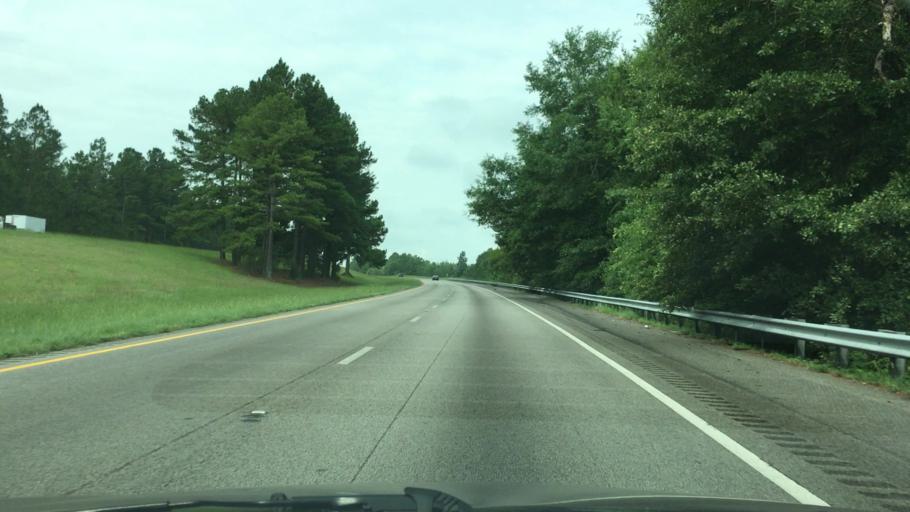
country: US
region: South Carolina
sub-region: Aiken County
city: Graniteville
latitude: 33.6250
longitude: -81.8180
